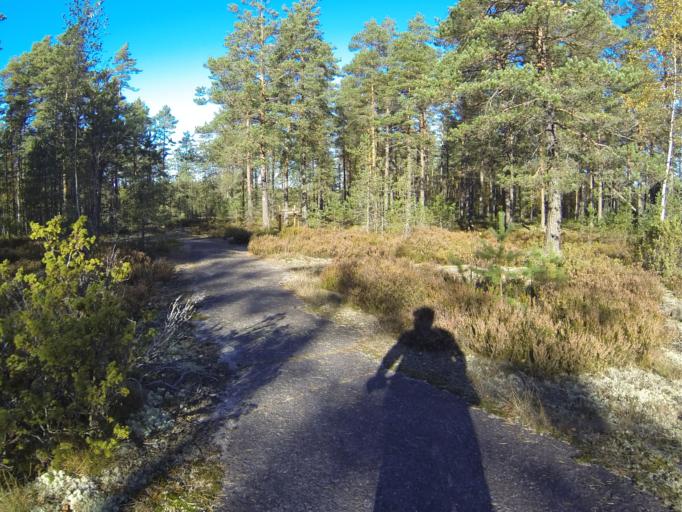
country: FI
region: Varsinais-Suomi
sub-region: Salo
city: Saerkisalo
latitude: 60.1997
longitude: 22.9241
